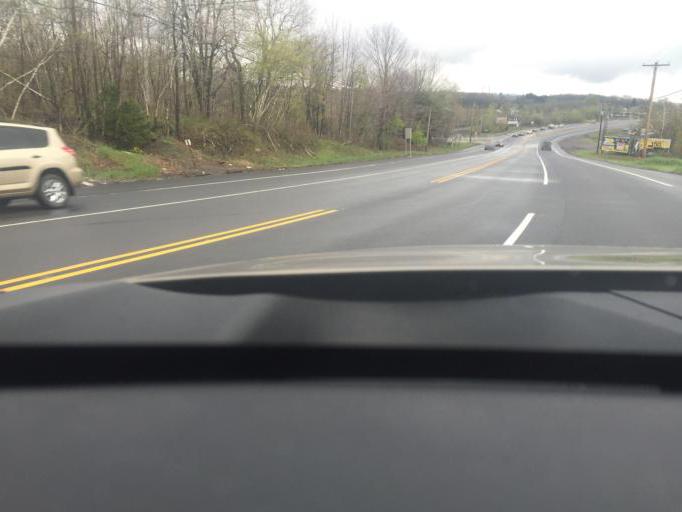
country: US
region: Pennsylvania
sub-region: Luzerne County
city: Harleigh
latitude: 40.9965
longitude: -75.9860
